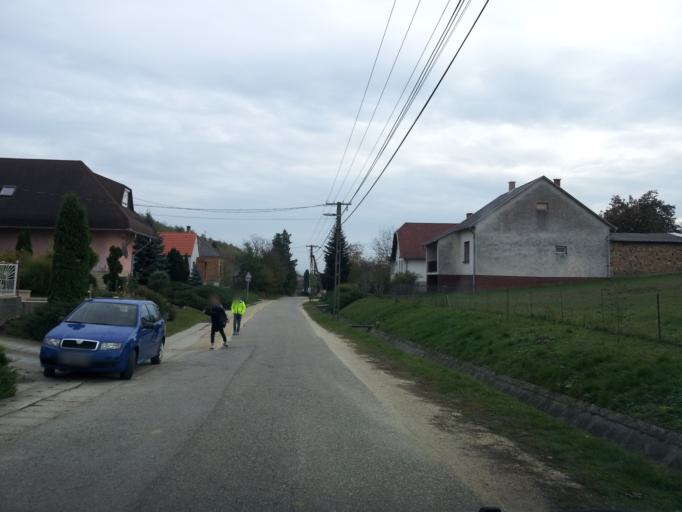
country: HU
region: Gyor-Moson-Sopron
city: Pannonhalma
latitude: 47.4854
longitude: 17.7006
